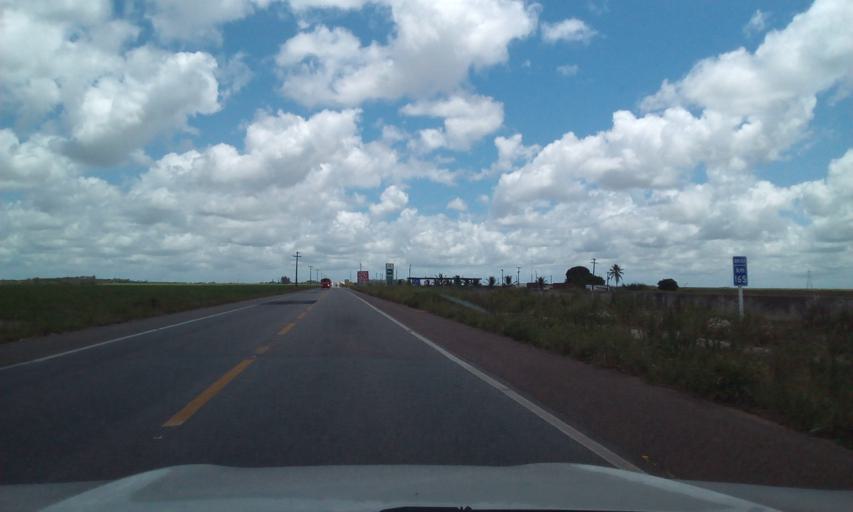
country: BR
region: Alagoas
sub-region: Campo Alegre
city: Campo Alegre
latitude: -9.9000
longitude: -36.2724
